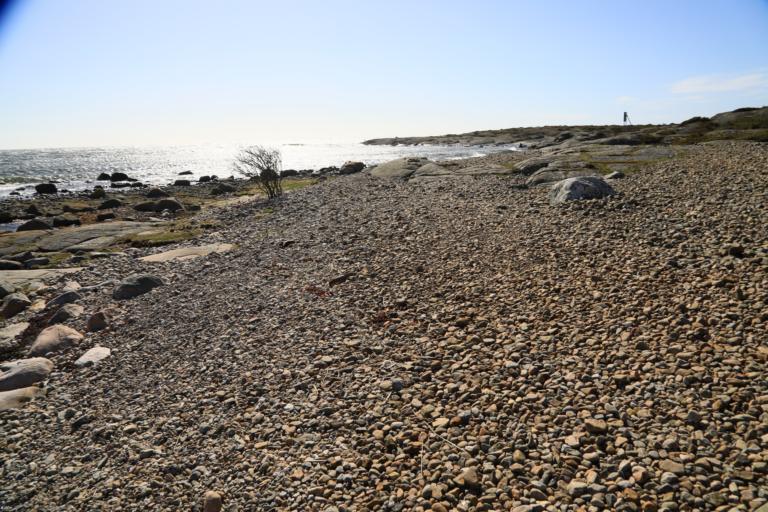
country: SE
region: Halland
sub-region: Varbergs Kommun
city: Varberg
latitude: 57.1165
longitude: 12.1991
